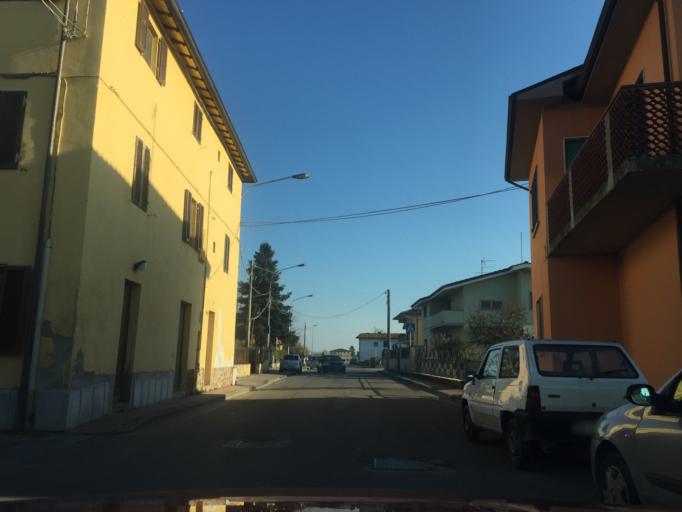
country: IT
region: Tuscany
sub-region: Provincia di Pistoia
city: Anchione
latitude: 43.8218
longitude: 10.7617
